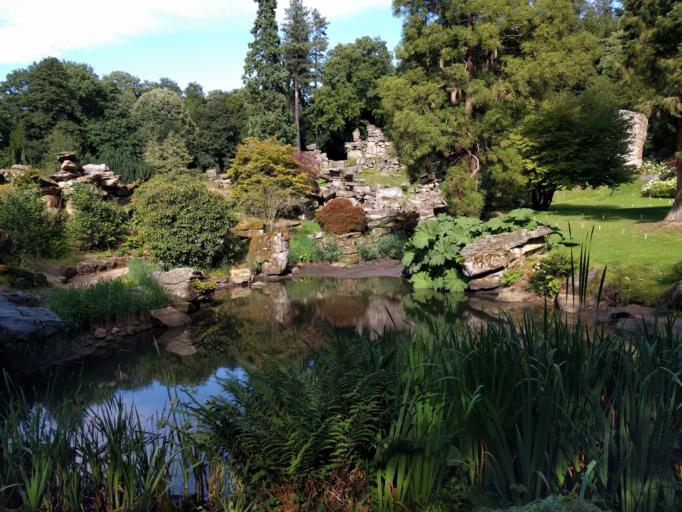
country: GB
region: England
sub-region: Derbyshire
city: Bakewell
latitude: 53.2252
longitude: -1.6095
